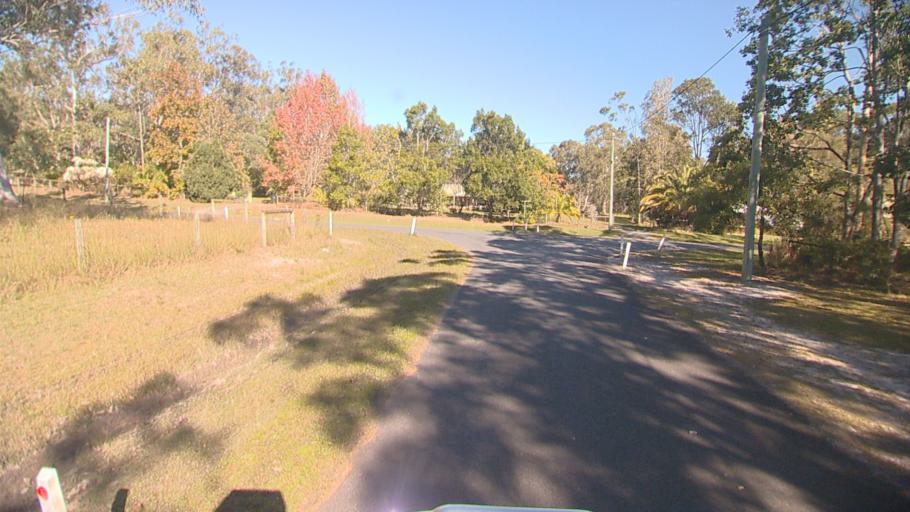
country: AU
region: Queensland
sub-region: Logan
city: Logan Reserve
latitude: -27.7212
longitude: 153.0692
